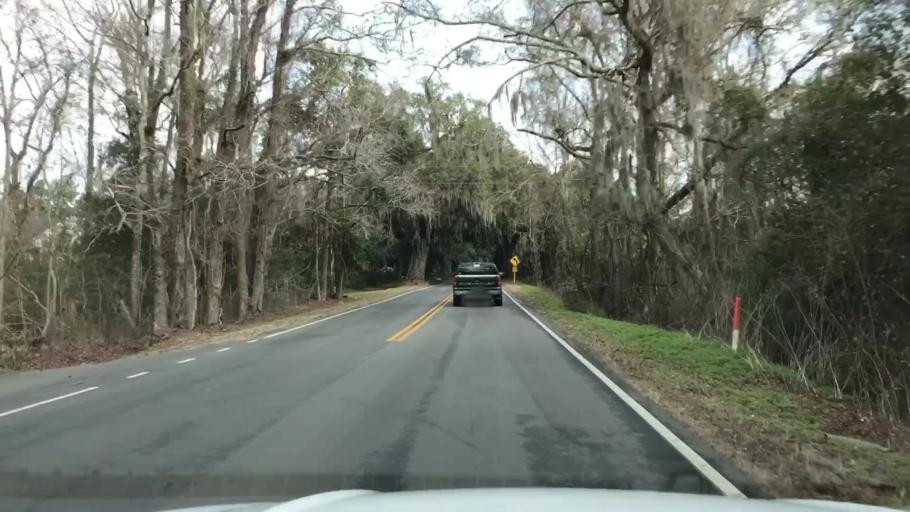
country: US
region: South Carolina
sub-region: Charleston County
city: Folly Beach
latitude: 32.6891
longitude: -80.0184
